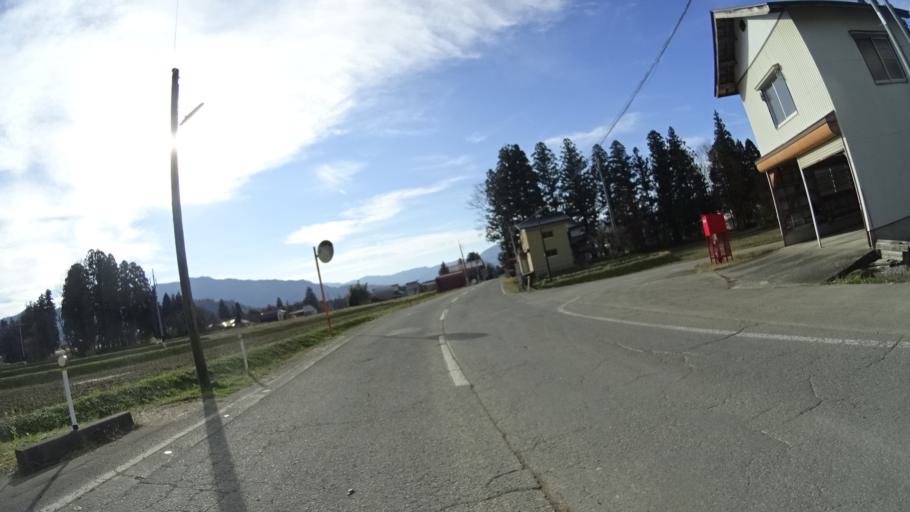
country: JP
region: Niigata
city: Shiozawa
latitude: 37.0153
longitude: 138.8833
